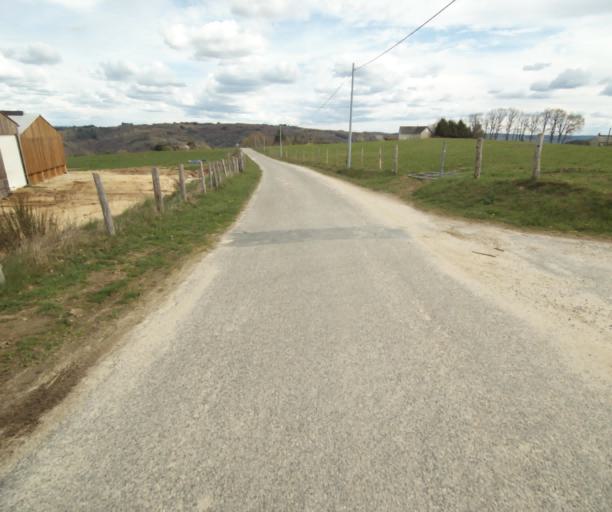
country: FR
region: Limousin
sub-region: Departement de la Correze
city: Argentat
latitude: 45.1819
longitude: 1.9422
